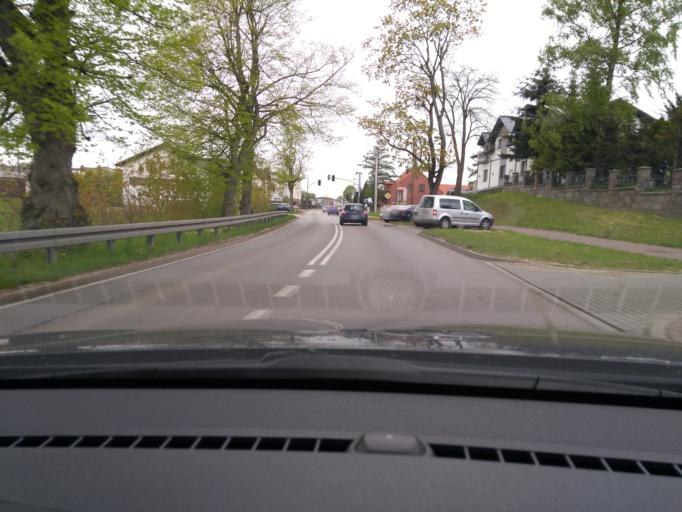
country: PL
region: Pomeranian Voivodeship
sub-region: Powiat kartuski
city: Sierakowice
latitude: 54.3423
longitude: 17.9016
